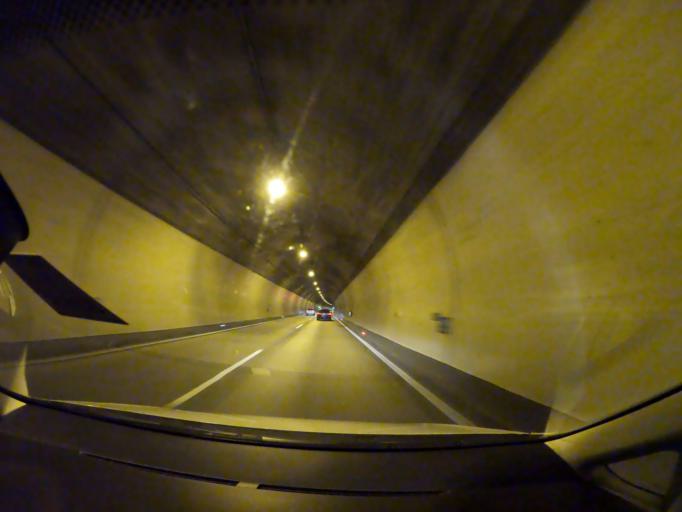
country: AT
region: Styria
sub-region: Politischer Bezirk Voitsberg
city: Pack
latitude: 46.9786
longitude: 14.9731
